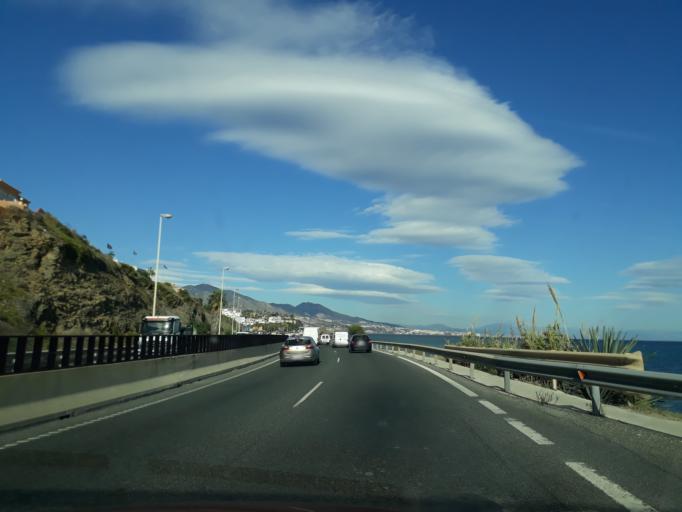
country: ES
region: Andalusia
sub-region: Provincia de Malaga
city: Fuengirola
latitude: 36.5086
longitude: -4.6372
